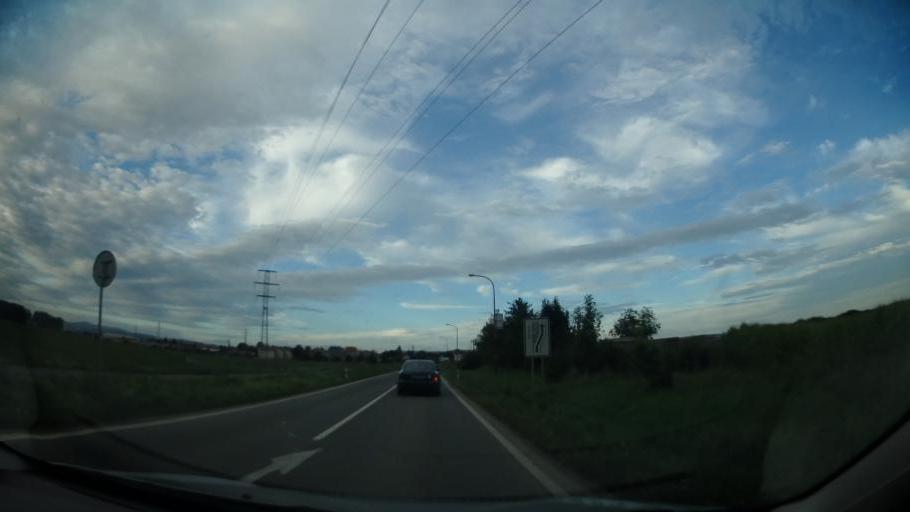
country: CZ
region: Olomoucky
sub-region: Okres Olomouc
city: Unicov
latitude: 49.7625
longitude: 17.1070
